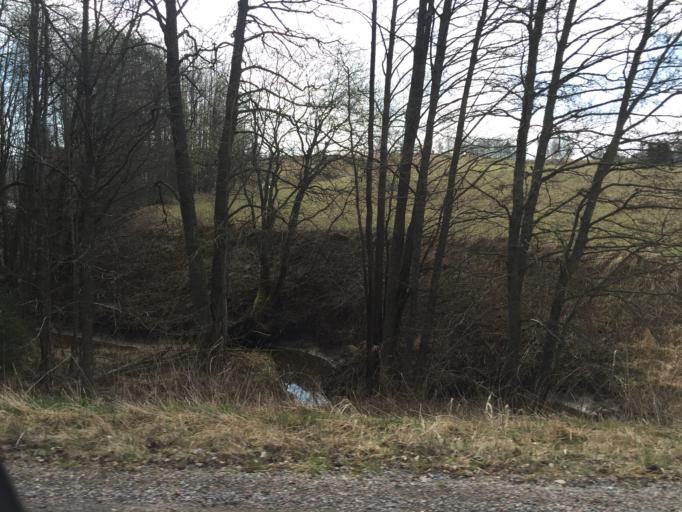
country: SE
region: Soedermanland
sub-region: Gnesta Kommun
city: Gnesta
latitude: 59.0268
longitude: 17.2009
